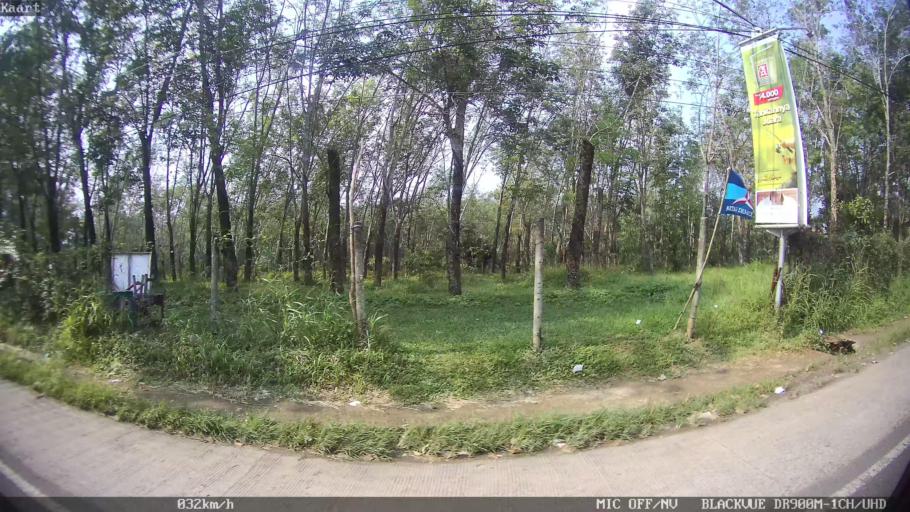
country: ID
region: Lampung
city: Gedongtataan
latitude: -5.3802
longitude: 105.1168
